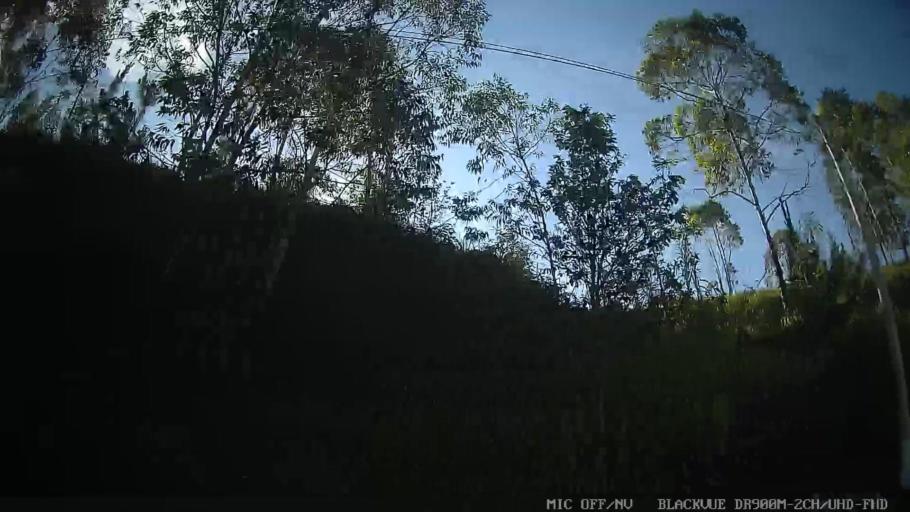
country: BR
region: Sao Paulo
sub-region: Serra Negra
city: Serra Negra
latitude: -22.6428
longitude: -46.6966
